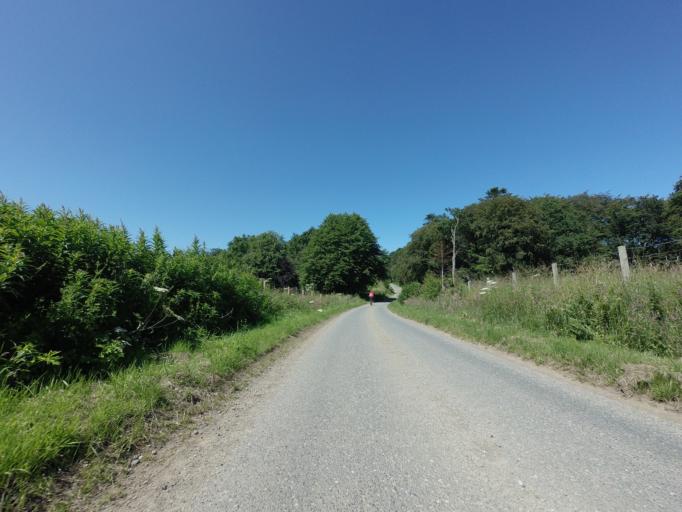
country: GB
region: Scotland
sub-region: Aberdeenshire
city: Macduff
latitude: 57.6425
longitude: -2.5057
